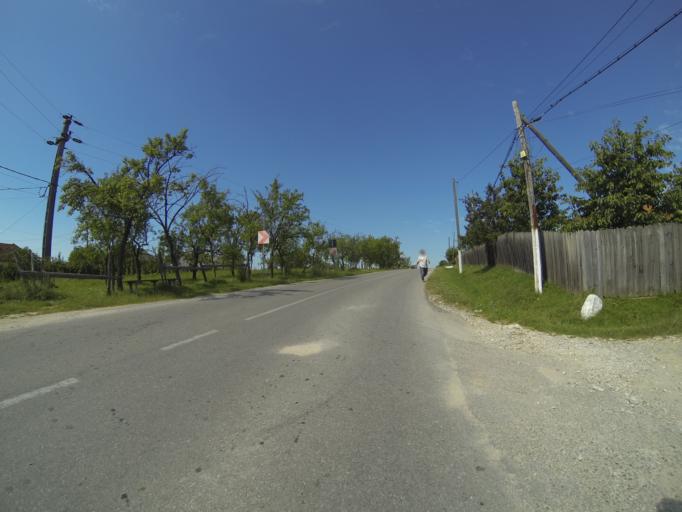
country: RO
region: Gorj
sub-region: Comuna Polovragi
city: Polovragi
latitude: 45.1654
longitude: 23.8275
